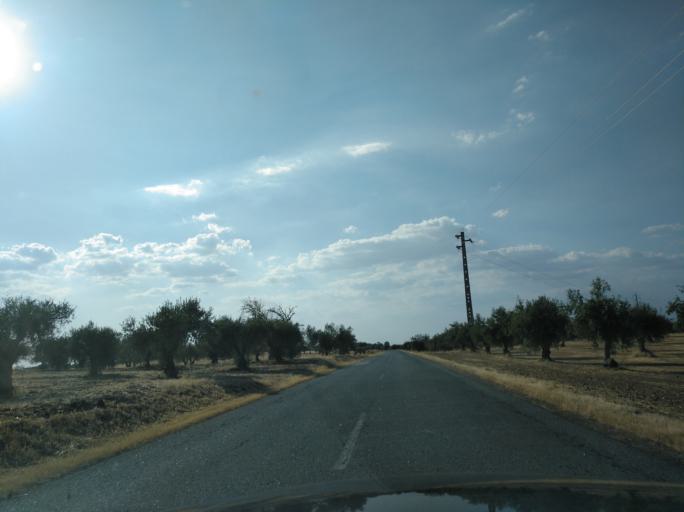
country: PT
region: Evora
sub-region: Mourao
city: Mourao
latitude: 38.3749
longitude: -7.3229
